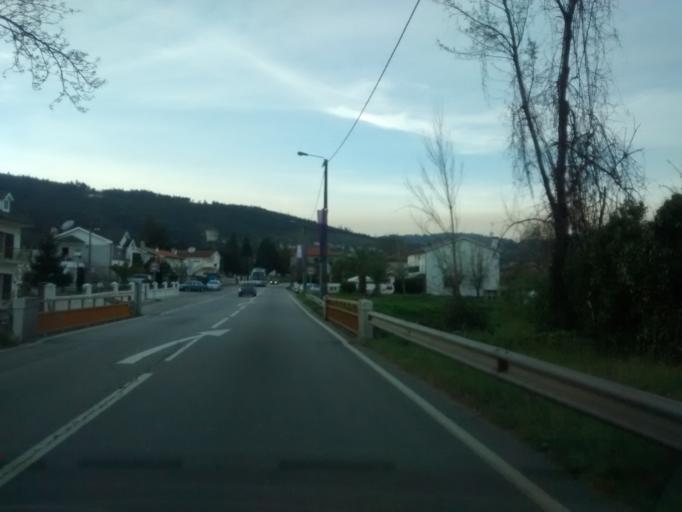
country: PT
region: Braga
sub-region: Guimaraes
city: Brito
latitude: 41.4898
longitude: -8.3591
